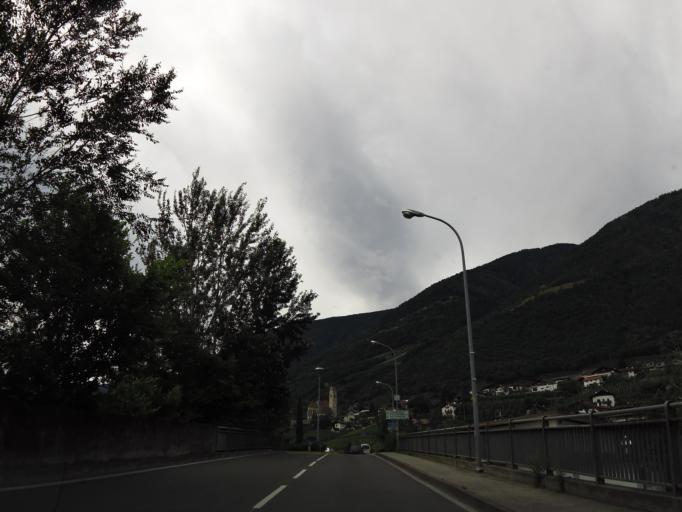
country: IT
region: Trentino-Alto Adige
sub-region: Bolzano
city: Marlengo
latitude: 46.6595
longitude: 11.1465
